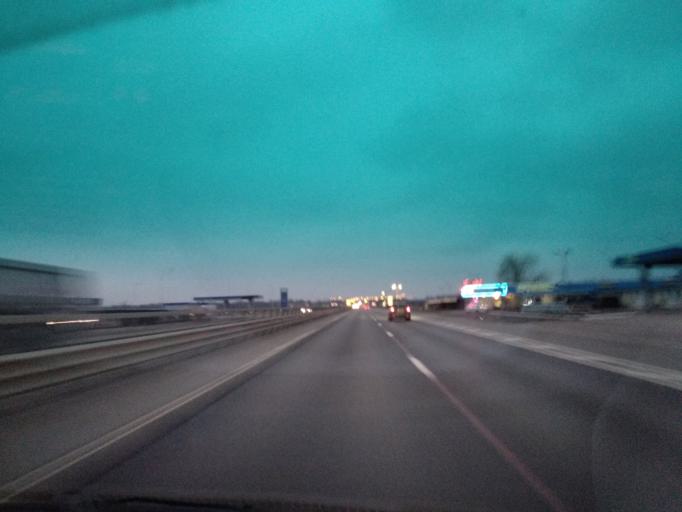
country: RU
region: Adygeya
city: Adygeysk
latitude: 44.8388
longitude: 39.2132
